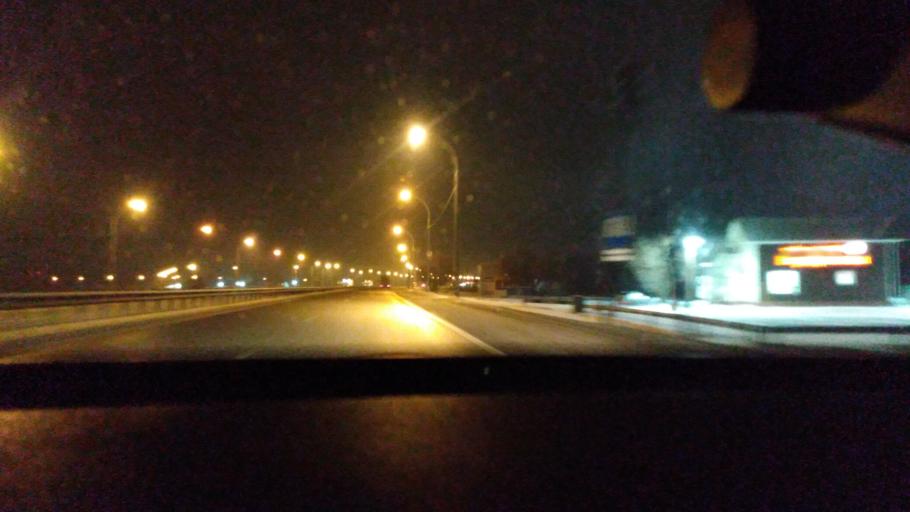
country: RU
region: Moskovskaya
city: Kolomna
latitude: 55.0947
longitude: 38.9037
